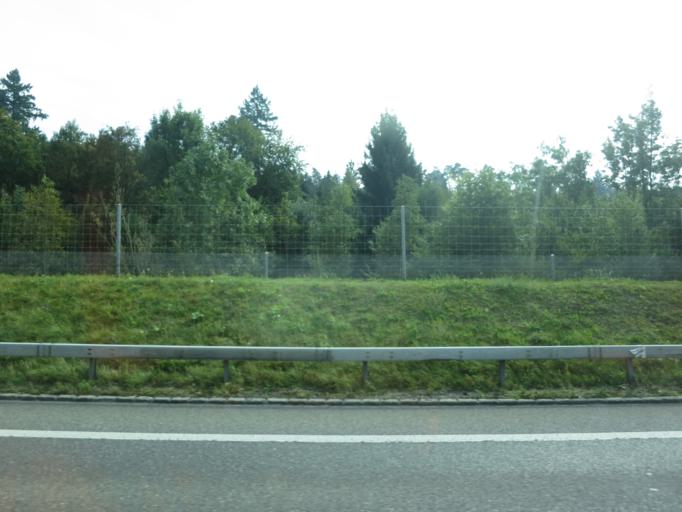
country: CH
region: Saint Gallen
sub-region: Wahlkreis See-Gaster
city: Eschenbach
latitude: 47.2313
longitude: 8.9072
